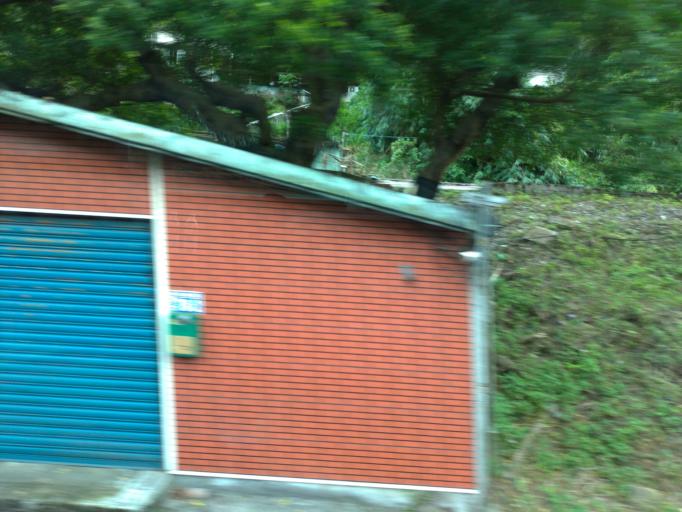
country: TW
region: Taiwan
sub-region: Keelung
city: Keelung
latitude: 25.1023
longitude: 121.7423
